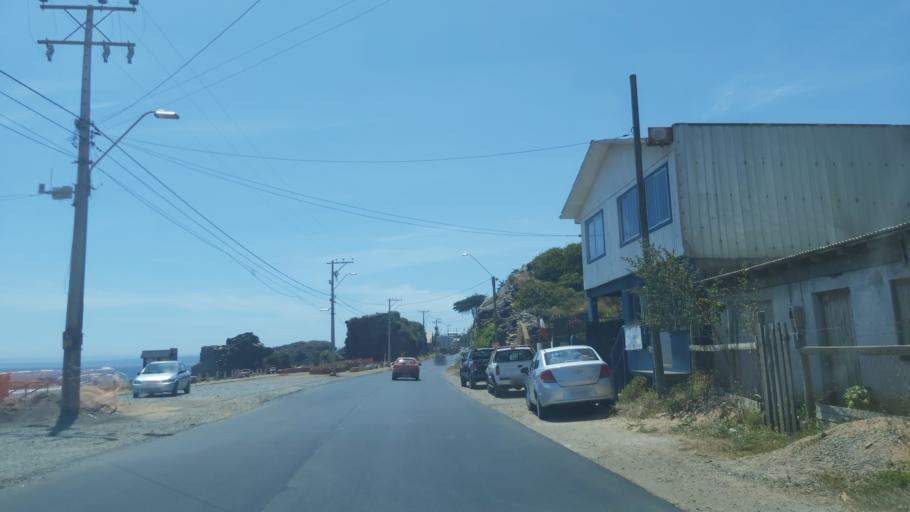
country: CL
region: Maule
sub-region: Provincia de Cauquenes
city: Cauquenes
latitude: -35.8217
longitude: -72.5994
